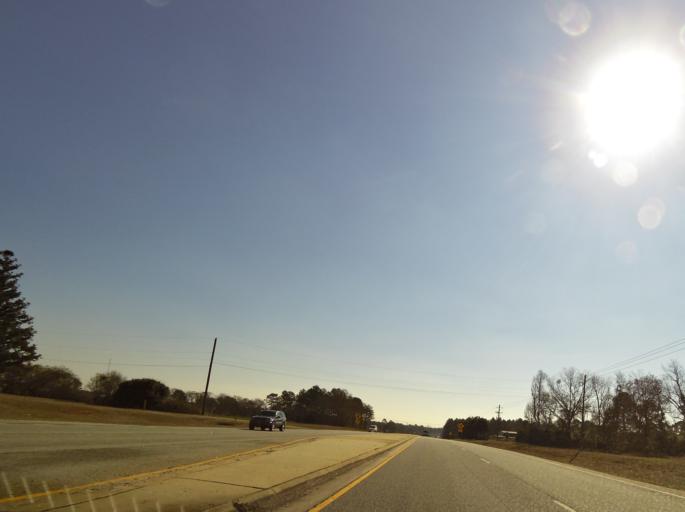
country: US
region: Georgia
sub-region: Pulaski County
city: Hawkinsville
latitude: 32.2981
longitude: -83.4903
